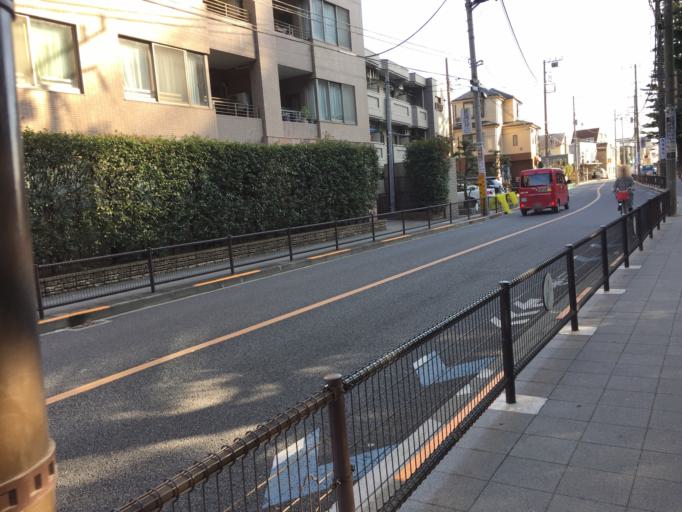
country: JP
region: Tokyo
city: Mitaka-shi
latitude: 35.6574
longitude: 139.6093
